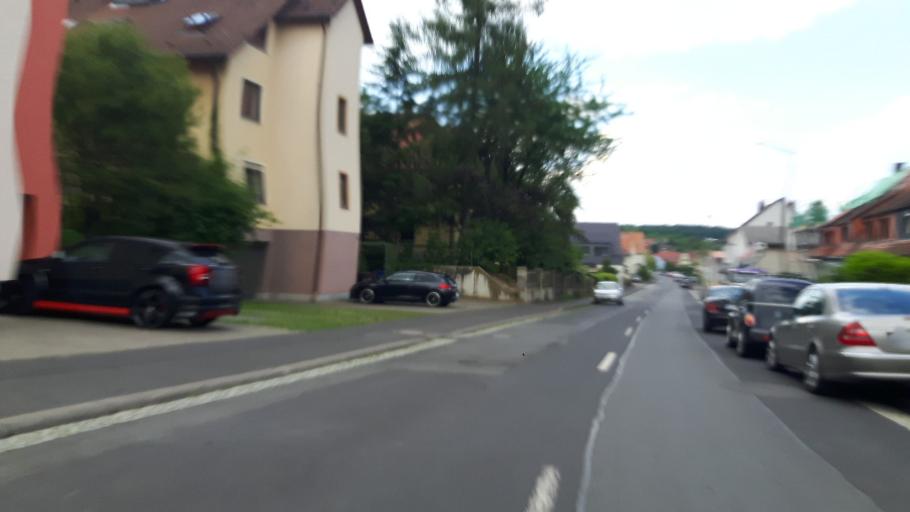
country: DE
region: Bavaria
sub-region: Regierungsbezirk Unterfranken
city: Reichenberg
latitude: 49.7275
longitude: 9.9152
